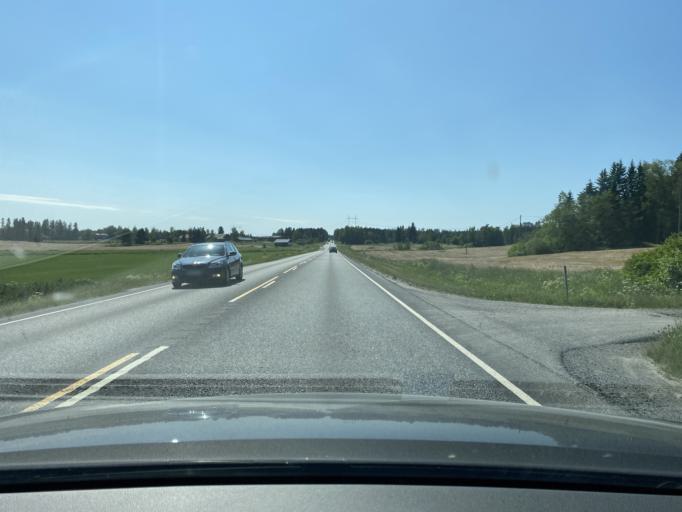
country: FI
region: Pirkanmaa
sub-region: Tampere
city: Nokia
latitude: 61.4188
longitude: 23.3259
